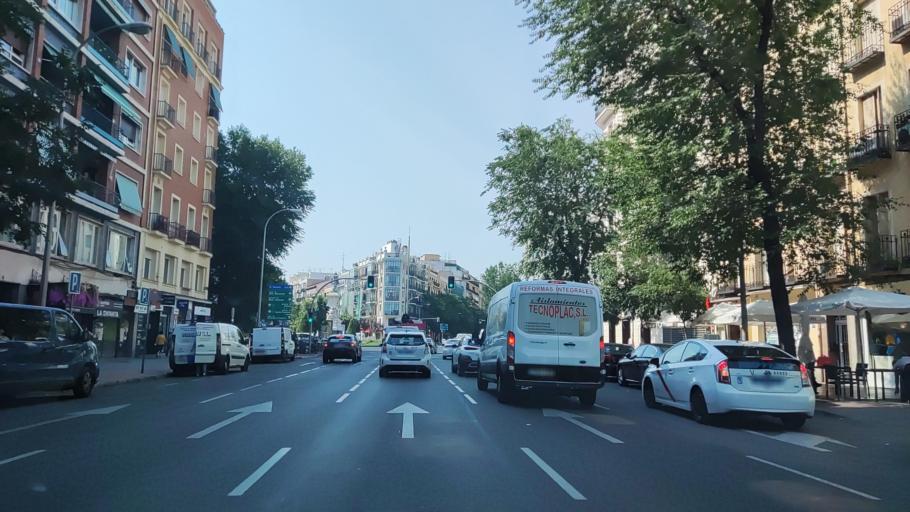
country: ES
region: Madrid
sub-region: Provincia de Madrid
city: Chamberi
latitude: 40.4345
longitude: -3.7044
